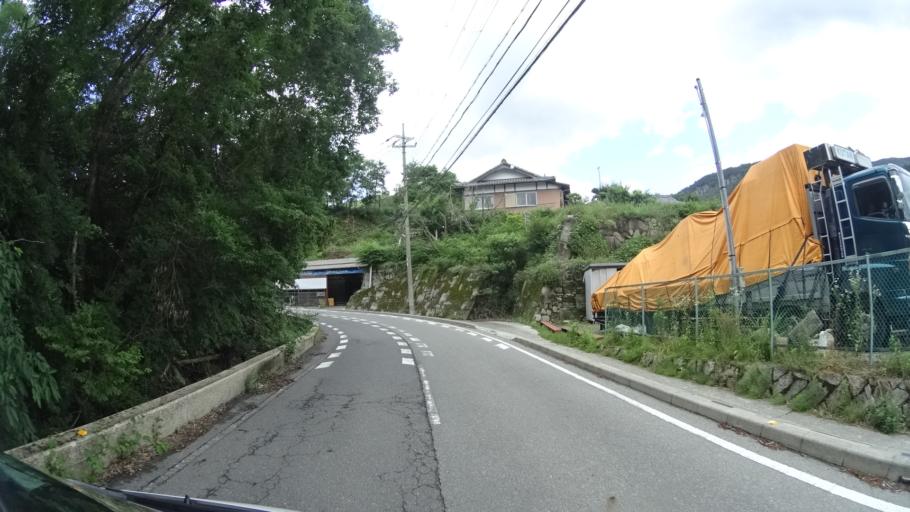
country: JP
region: Kyoto
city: Kameoka
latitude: 35.0156
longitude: 135.4274
